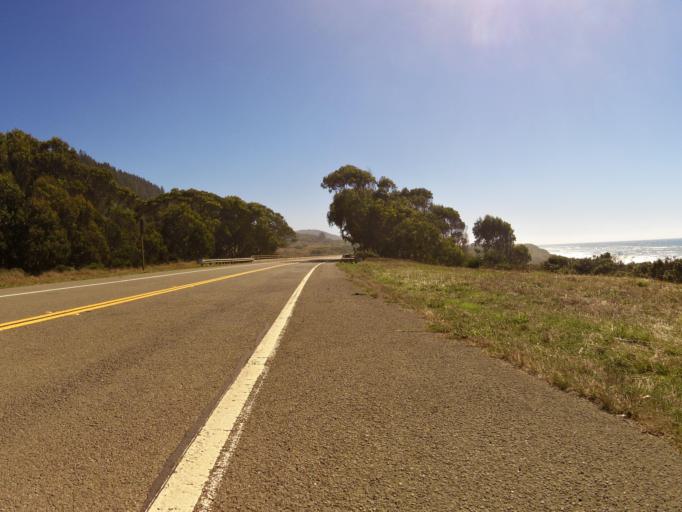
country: US
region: California
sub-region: Mendocino County
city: Fort Bragg
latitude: 39.6792
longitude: -123.7902
